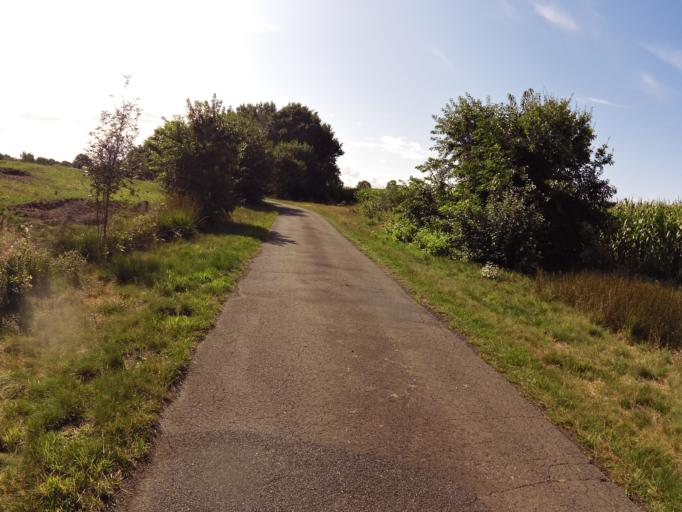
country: DE
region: Lower Saxony
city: Sandbostel
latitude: 53.3909
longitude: 9.1212
